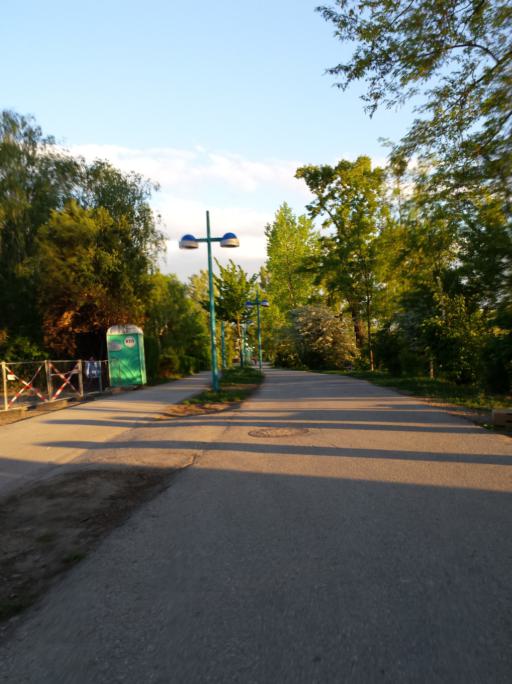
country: AT
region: Vienna
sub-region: Wien Stadt
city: Vienna
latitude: 48.2185
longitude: 16.4365
